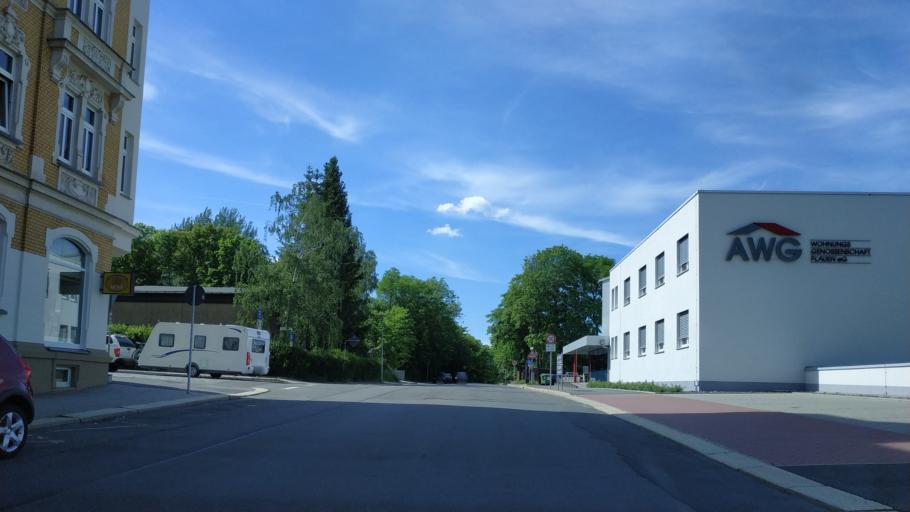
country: DE
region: Saxony
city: Plauen
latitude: 50.5093
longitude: 12.1354
